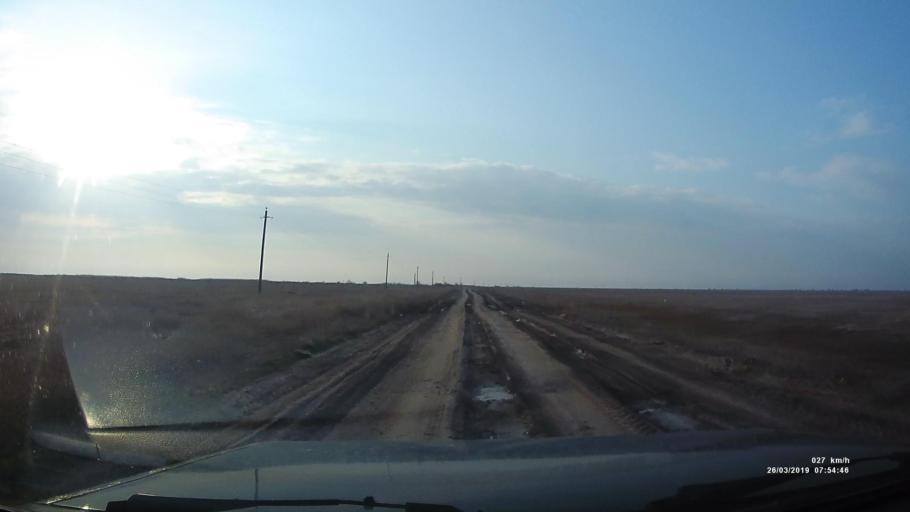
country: RU
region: Krasnodarskiy
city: Shabel'skoye
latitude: 47.1314
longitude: 38.5525
